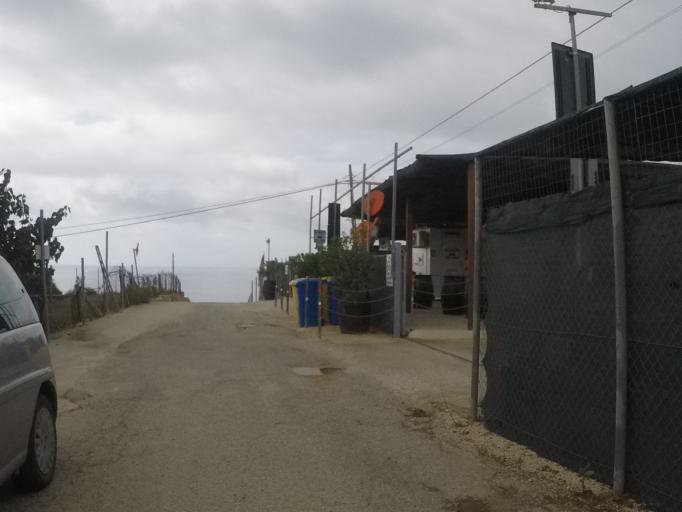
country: IT
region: Sicily
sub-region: Agrigento
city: Realmonte
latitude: 37.2897
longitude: 13.4789
